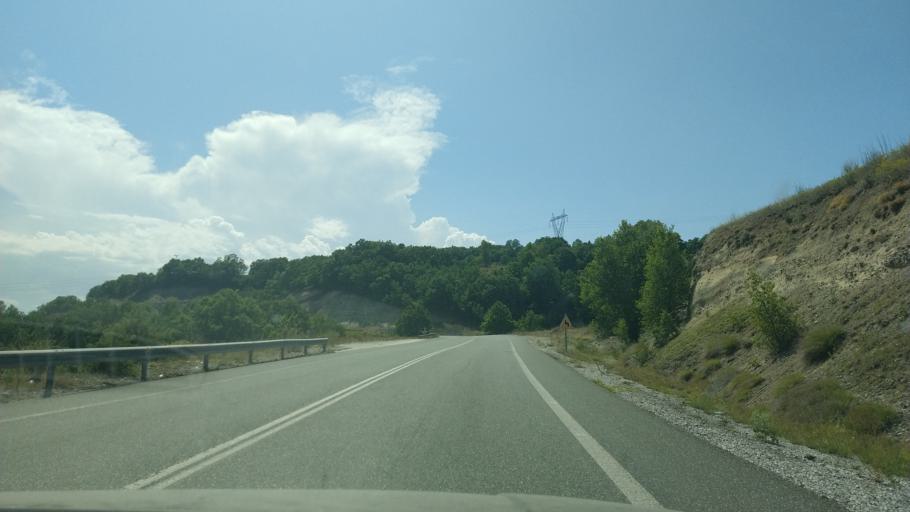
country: GR
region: West Macedonia
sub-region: Nomos Grevenon
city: Grevena
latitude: 40.0506
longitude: 21.4758
